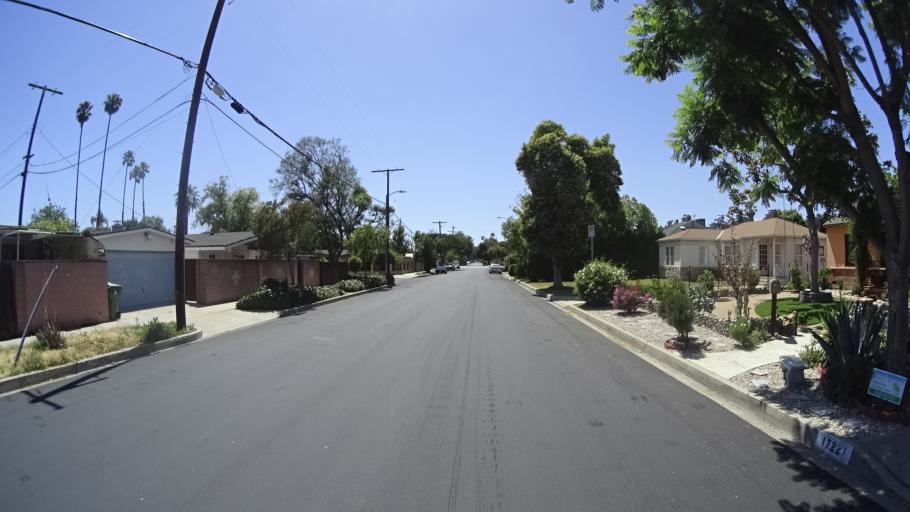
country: US
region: California
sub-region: Los Angeles County
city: Northridge
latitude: 34.1894
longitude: -118.5083
